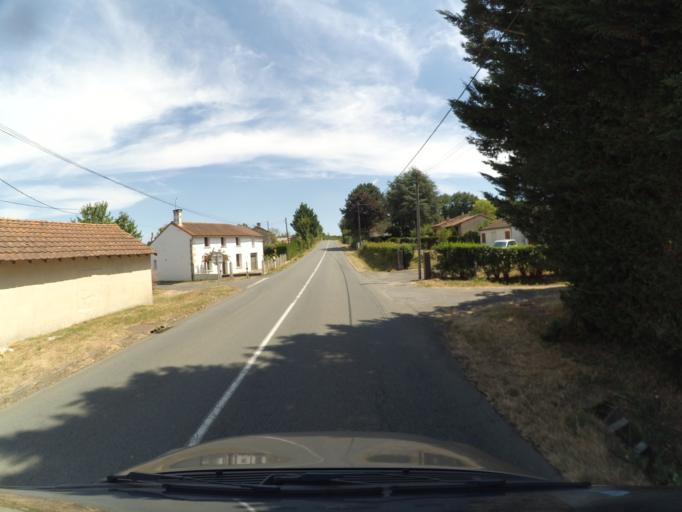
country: FR
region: Poitou-Charentes
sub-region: Departement de la Vienne
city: Usson-du-Poitou
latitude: 46.3279
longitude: 0.4766
